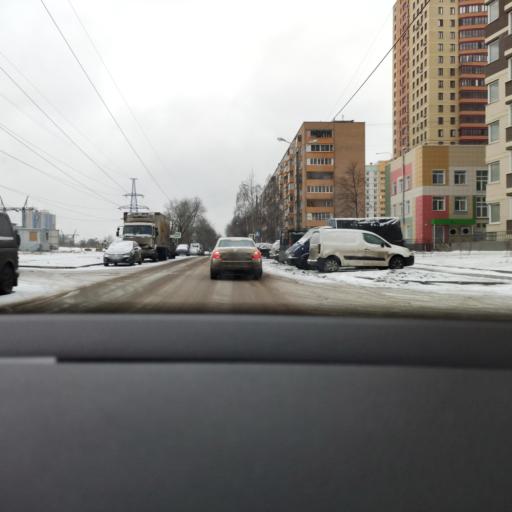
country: RU
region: Moskovskaya
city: Reutov
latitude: 55.7694
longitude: 37.8546
